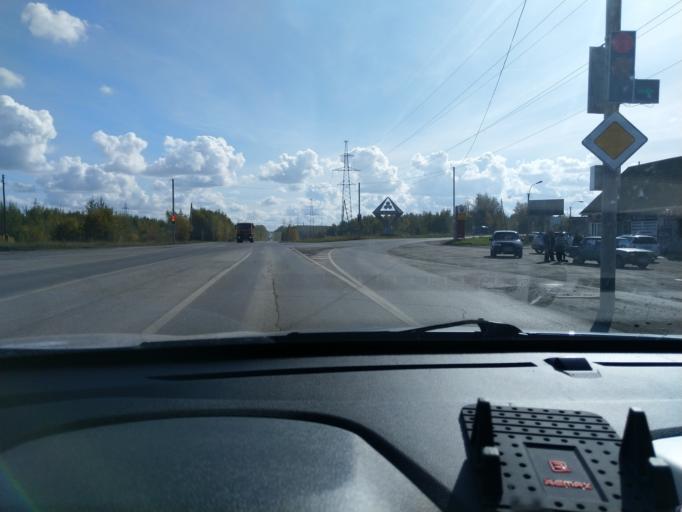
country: RU
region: Perm
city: Berezniki
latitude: 59.4644
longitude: 56.8450
